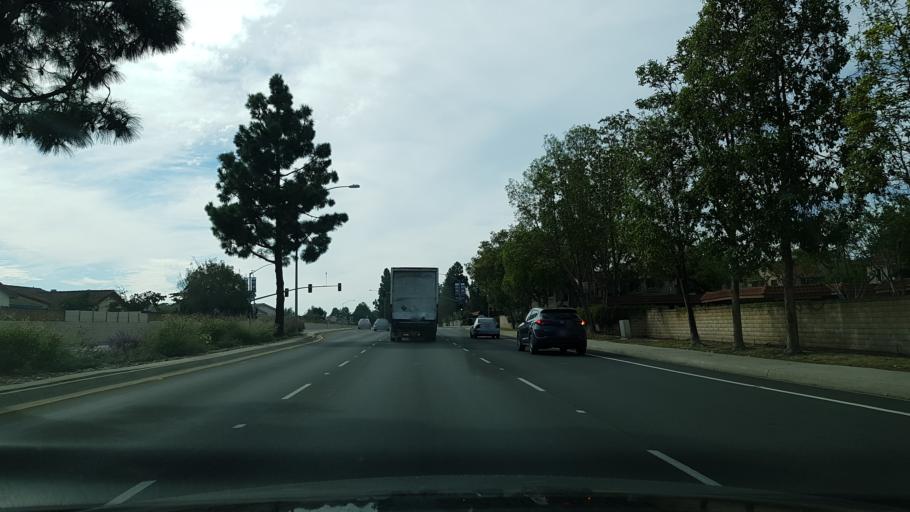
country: US
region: California
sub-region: San Diego County
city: Fairbanks Ranch
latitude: 32.9095
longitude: -117.1606
